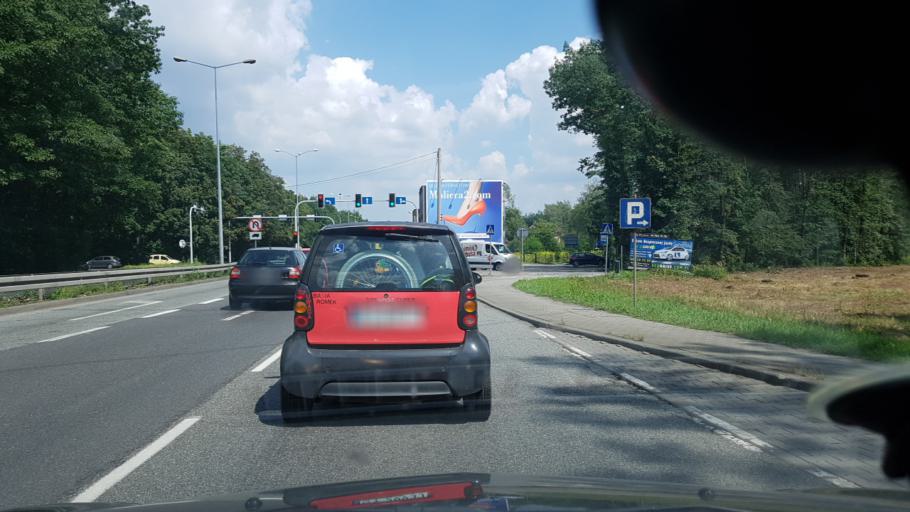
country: PL
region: Silesian Voivodeship
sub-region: Powiat mikolowski
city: Mikolow
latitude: 50.1955
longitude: 18.9310
